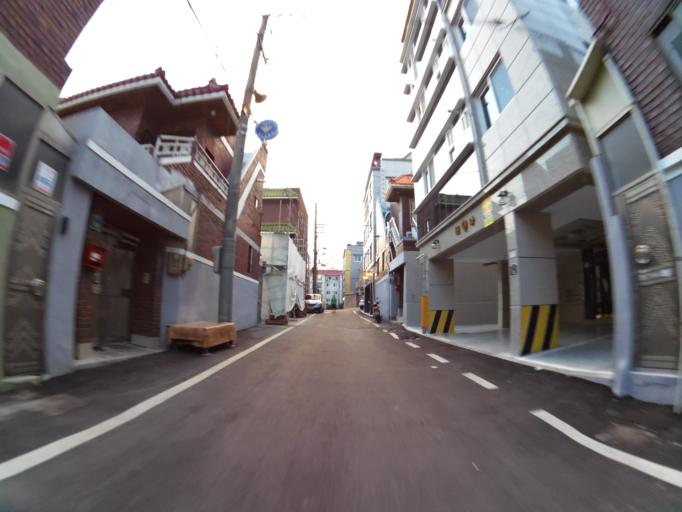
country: KR
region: Gyeongsangbuk-do
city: Gyeongsan-si
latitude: 35.8405
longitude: 128.7562
